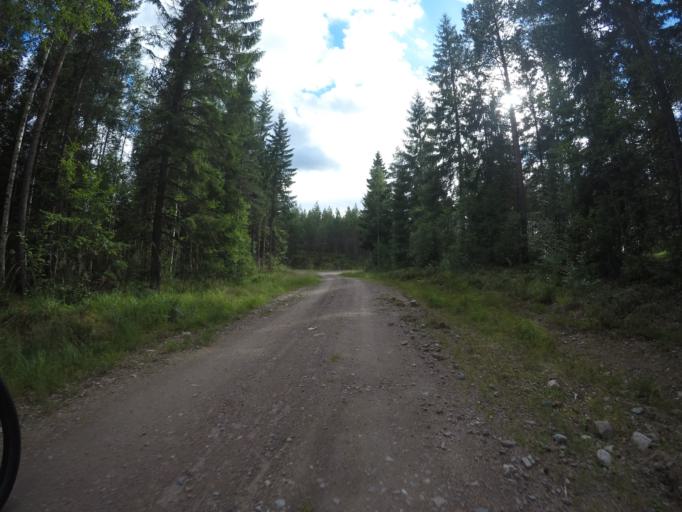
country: SE
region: Vaermland
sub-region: Filipstads Kommun
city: Lesjofors
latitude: 60.0425
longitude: 14.3728
